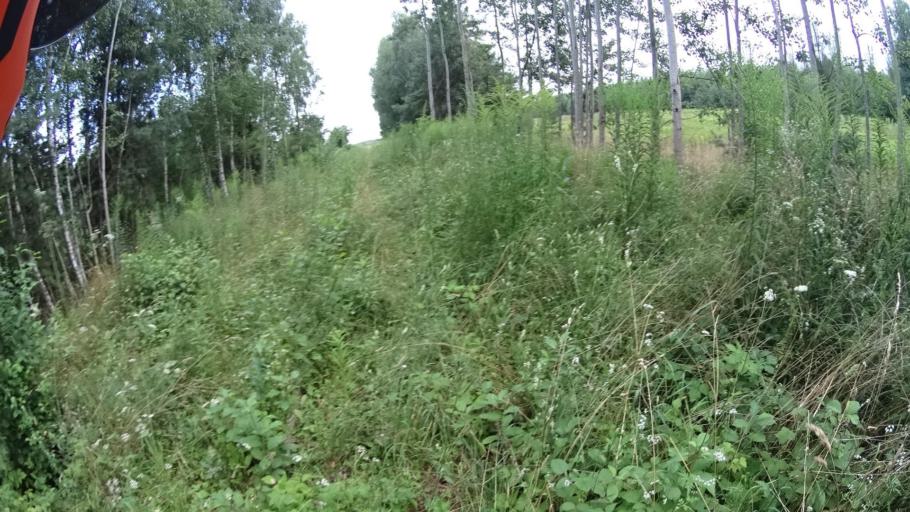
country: PL
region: Masovian Voivodeship
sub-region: Powiat piaseczynski
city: Tarczyn
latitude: 51.9674
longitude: 20.8688
